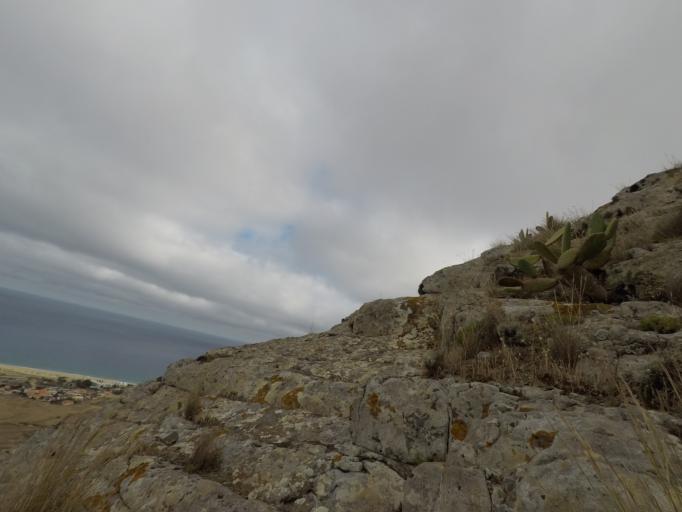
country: PT
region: Madeira
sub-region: Porto Santo
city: Vila de Porto Santo
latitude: 33.0462
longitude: -16.3686
